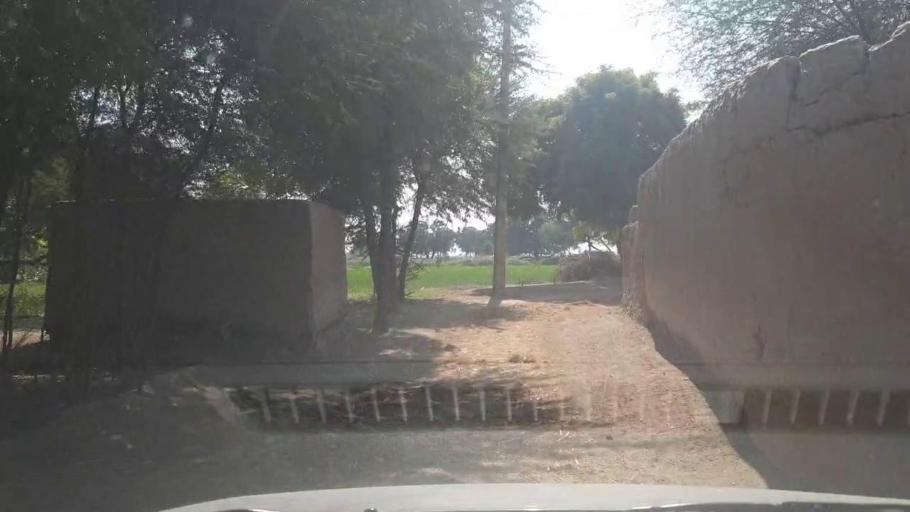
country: PK
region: Sindh
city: Chambar
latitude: 25.2513
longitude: 68.8203
